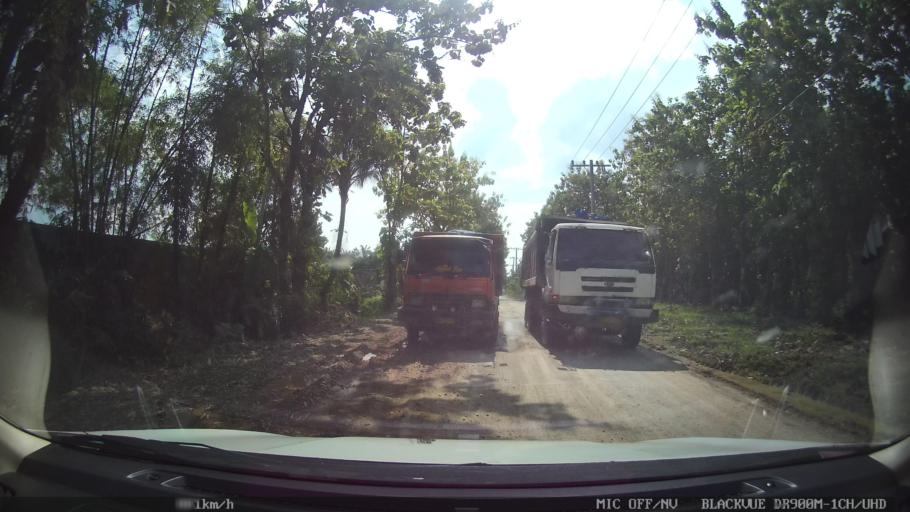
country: ID
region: North Sumatra
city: Binjai
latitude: 3.6344
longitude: 98.5285
